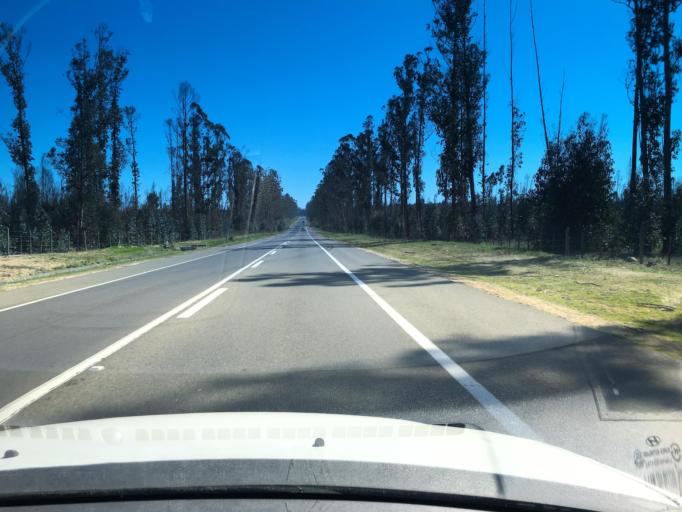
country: CL
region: Valparaiso
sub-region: San Antonio Province
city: El Tabo
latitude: -33.4040
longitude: -71.5711
